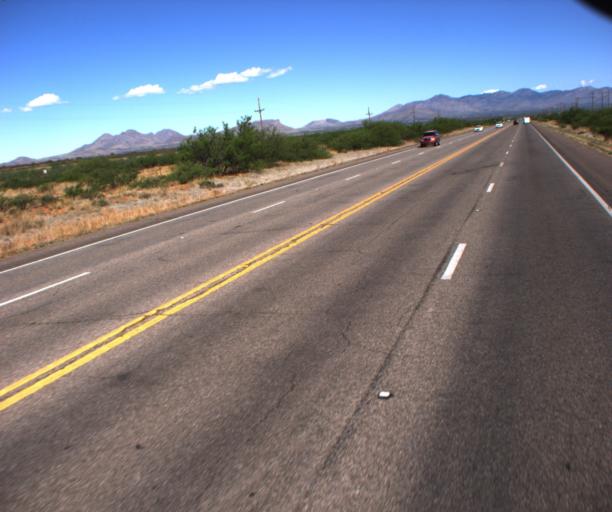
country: US
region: Arizona
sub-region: Cochise County
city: Huachuca City
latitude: 31.6000
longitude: -110.3271
